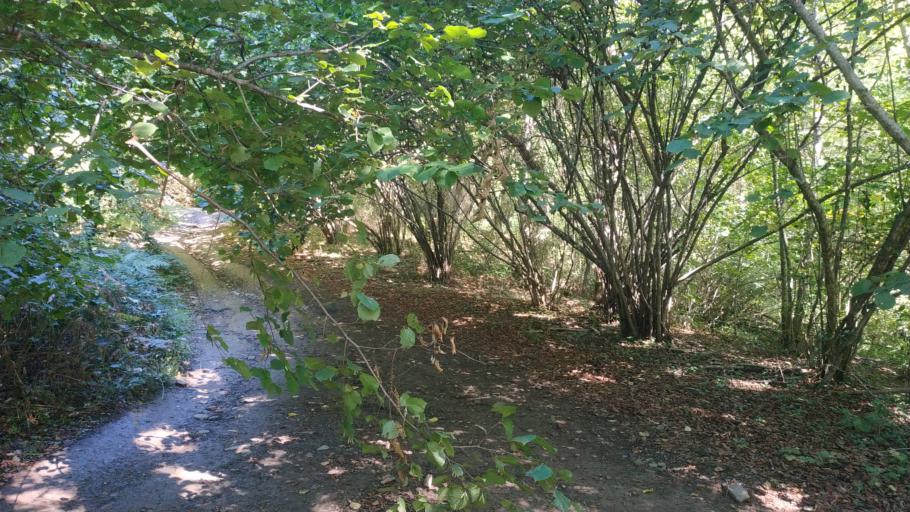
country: RU
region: Krasnodarskiy
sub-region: Sochi City
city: Lazarevskoye
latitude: 43.9799
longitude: 39.4198
